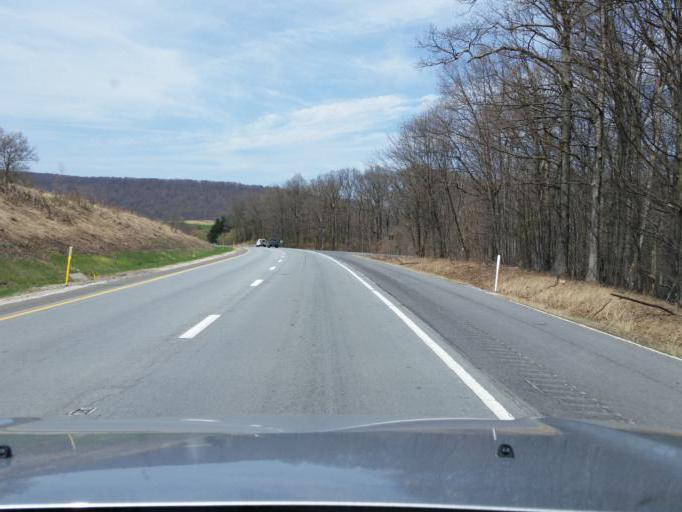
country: US
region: Pennsylvania
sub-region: Perry County
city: Newport
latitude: 40.4913
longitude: -77.0781
